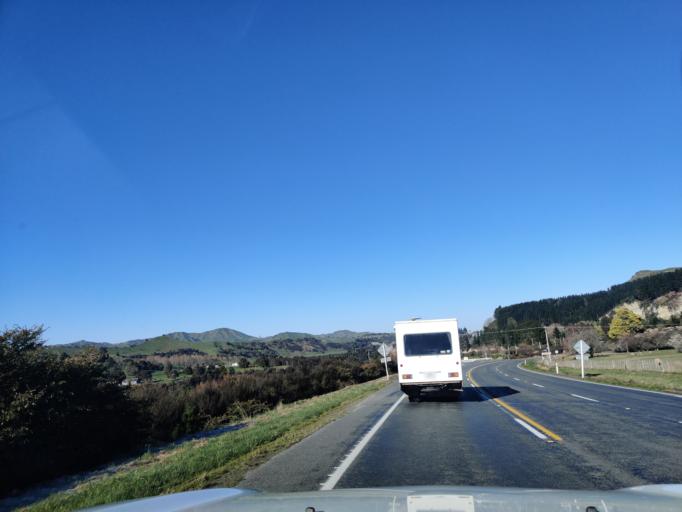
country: NZ
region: Manawatu-Wanganui
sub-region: Ruapehu District
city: Waiouru
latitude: -39.7505
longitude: 175.8347
